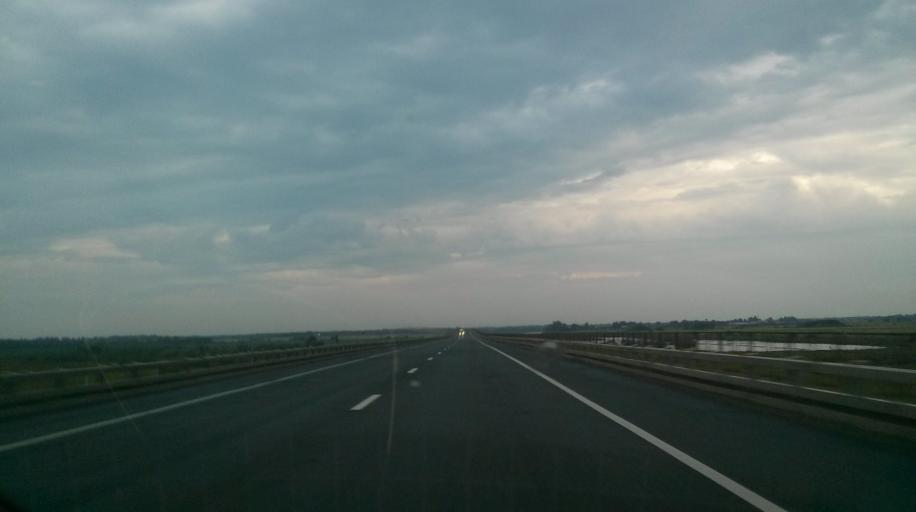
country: RU
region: Vladimir
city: Murom
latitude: 55.5949
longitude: 42.1108
